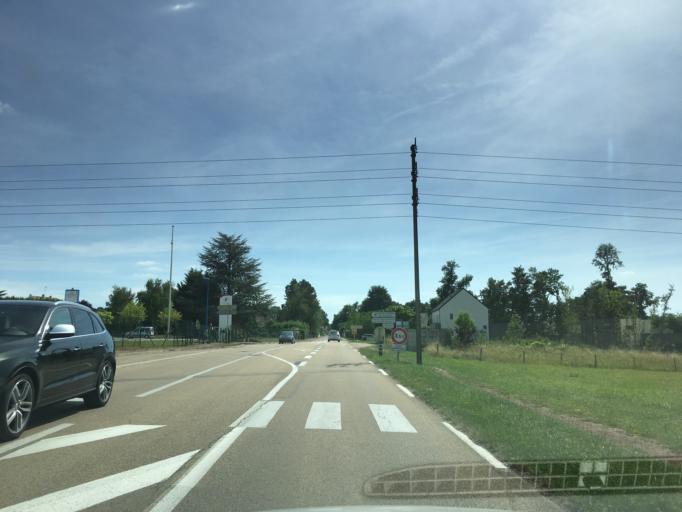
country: FR
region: Bourgogne
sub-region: Departement de l'Yonne
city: Saint-Georges-sur-Baulche
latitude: 47.8133
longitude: 3.5373
